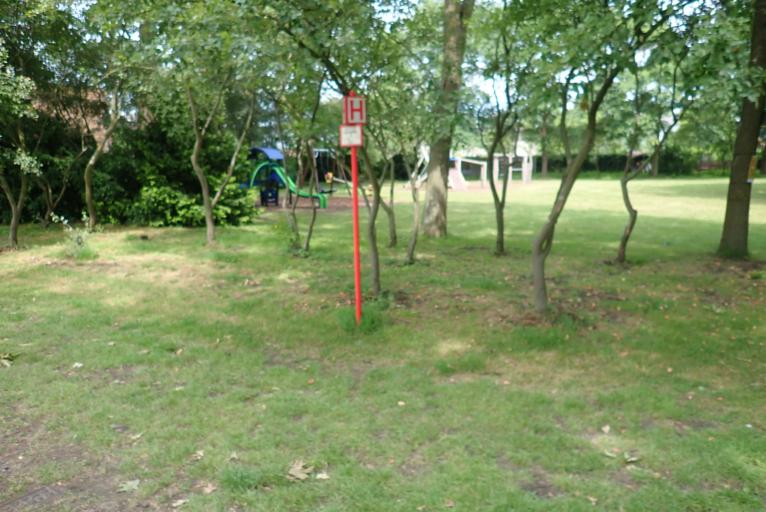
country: BE
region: Flanders
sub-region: Provincie Antwerpen
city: Zandhoven
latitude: 51.2171
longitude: 4.6976
